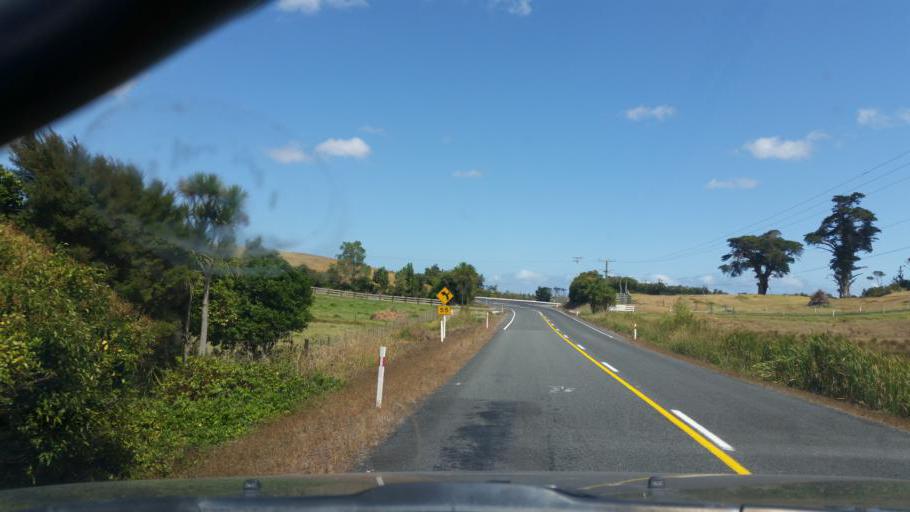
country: NZ
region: Northland
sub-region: Kaipara District
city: Dargaville
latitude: -35.9095
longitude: 173.8433
